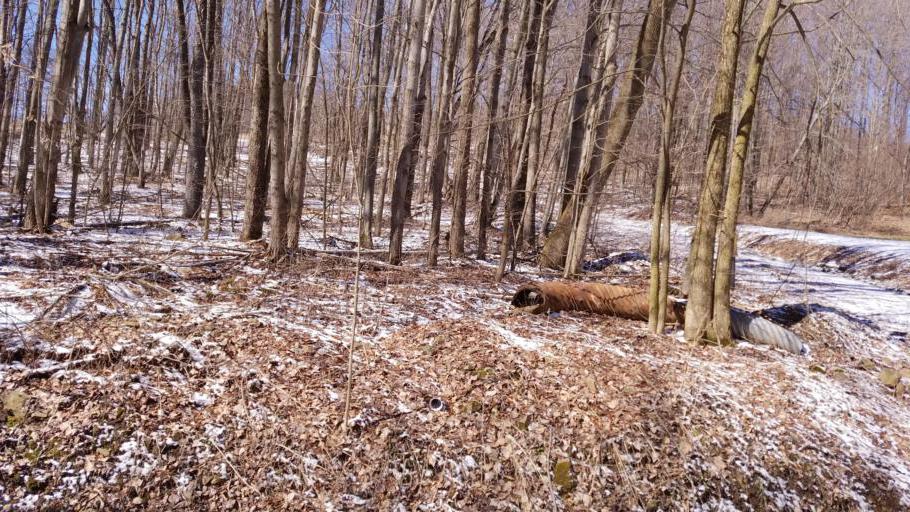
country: US
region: Pennsylvania
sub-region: Tioga County
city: Westfield
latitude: 41.9439
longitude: -77.7304
